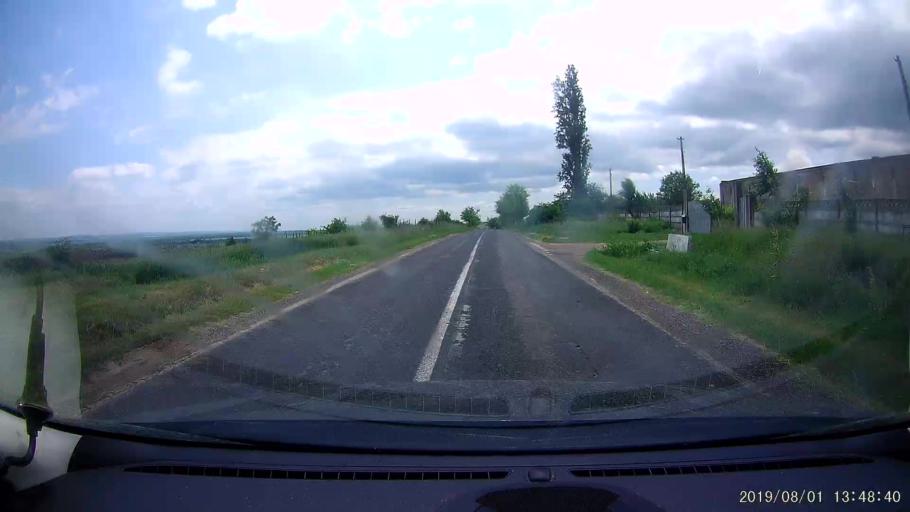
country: RO
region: Galati
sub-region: Comuna Oancea
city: Oancea
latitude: 45.9045
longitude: 28.1107
